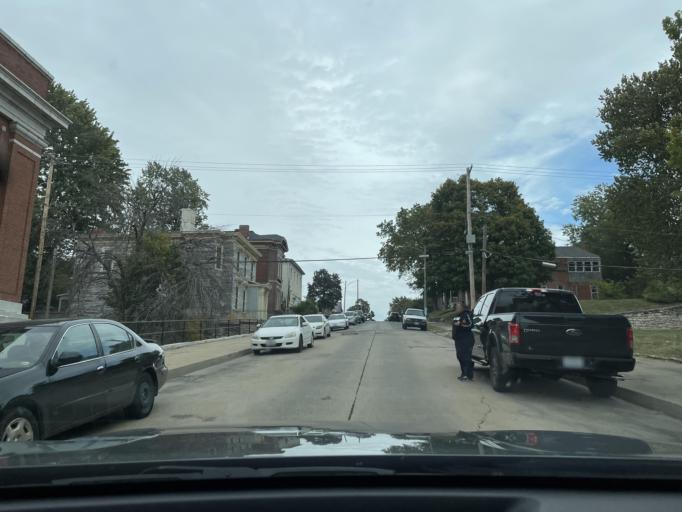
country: US
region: Missouri
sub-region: Buchanan County
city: Saint Joseph
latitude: 39.7651
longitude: -94.8478
